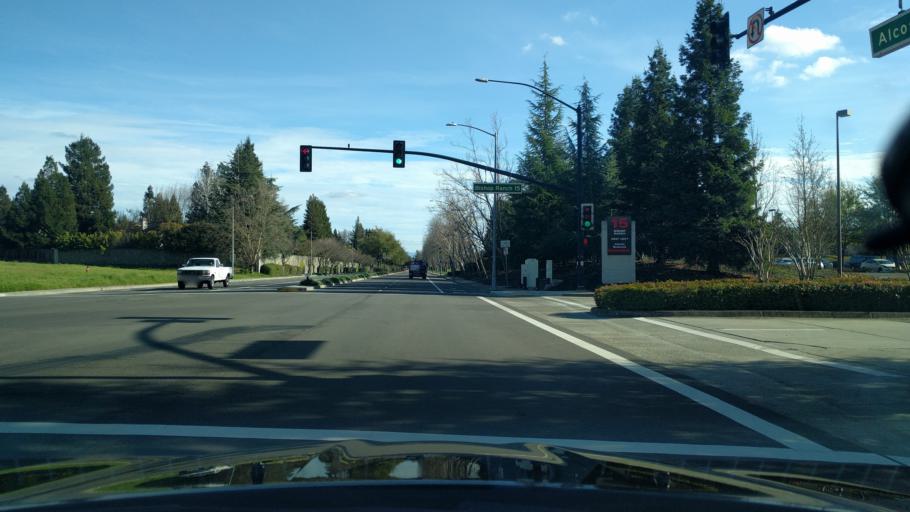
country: US
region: California
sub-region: Contra Costa County
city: San Ramon
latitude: 37.7732
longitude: -121.9586
